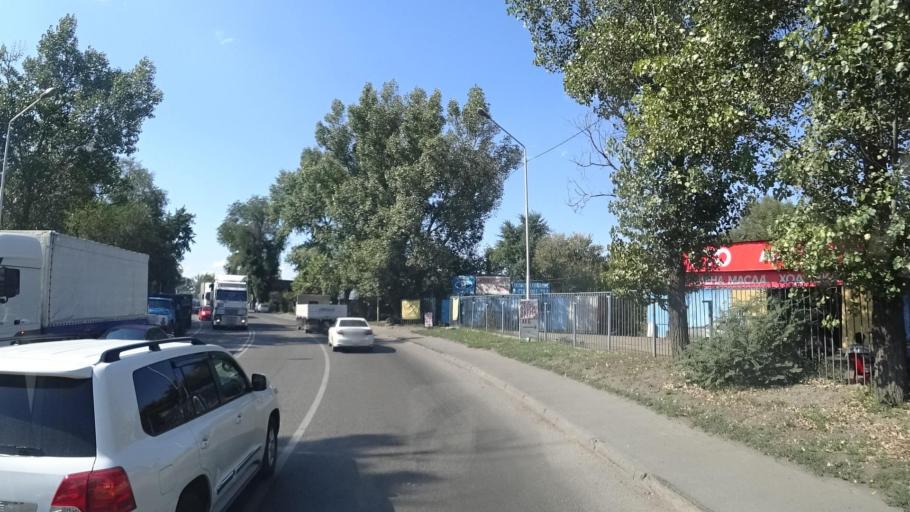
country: KZ
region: Almaty Oblysy
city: Pervomayskiy
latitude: 43.3502
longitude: 76.9633
